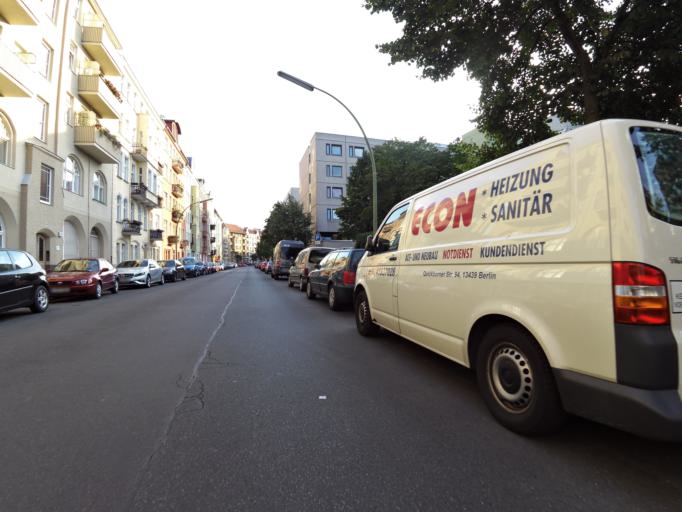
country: DE
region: Berlin
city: Berlin Schoeneberg
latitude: 52.4813
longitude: 13.3536
